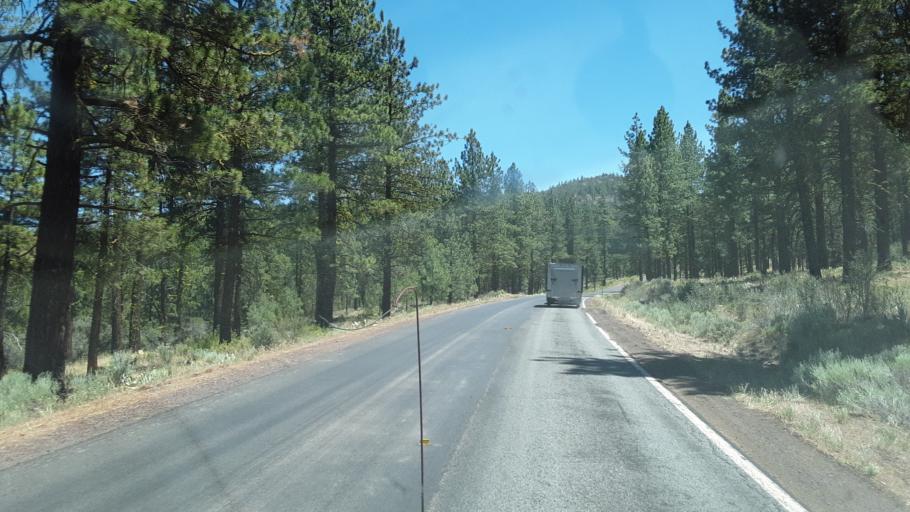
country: US
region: California
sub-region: Modoc County
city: Alturas
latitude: 40.9771
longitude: -120.7808
